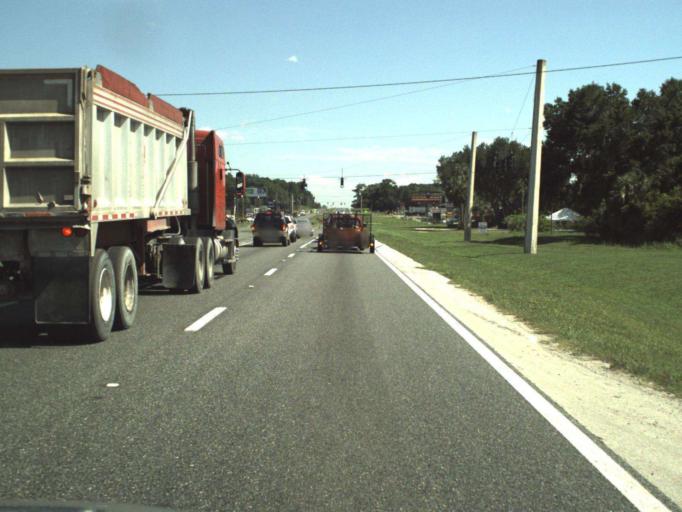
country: US
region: Florida
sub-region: Marion County
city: Belleview
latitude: 29.0888
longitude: -82.0816
